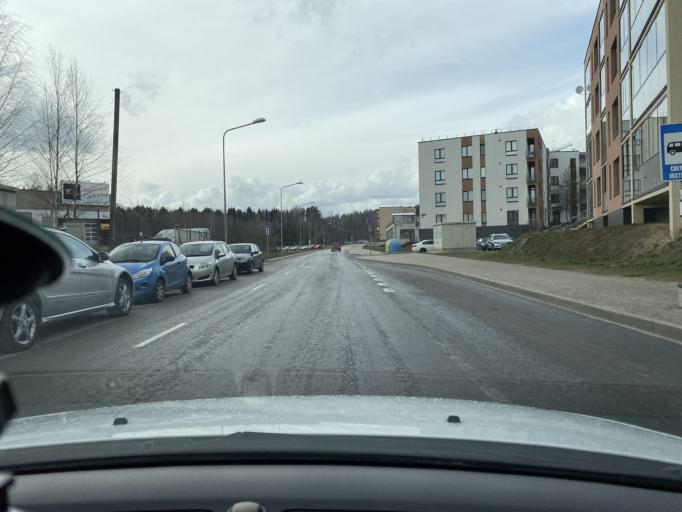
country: LT
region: Vilnius County
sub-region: Vilnius
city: Fabijoniskes
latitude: 54.7550
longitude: 25.2618
